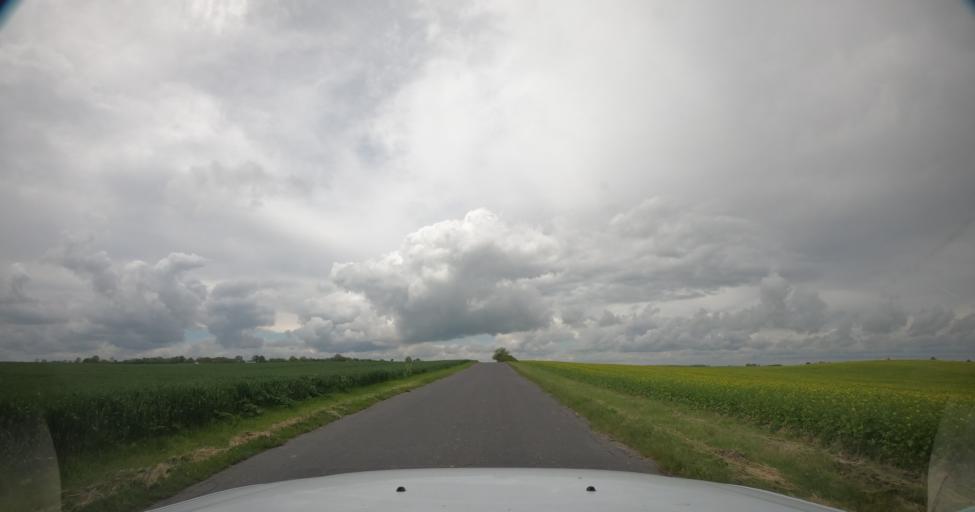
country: PL
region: West Pomeranian Voivodeship
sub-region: Powiat pyrzycki
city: Kozielice
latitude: 53.0785
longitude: 14.8666
